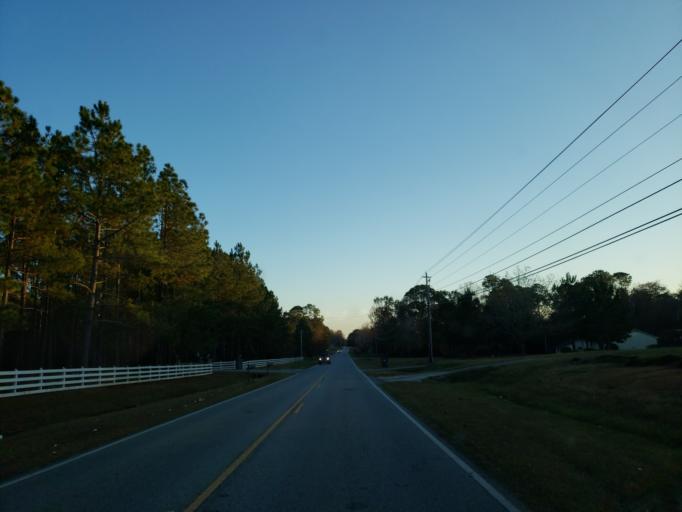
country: US
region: Georgia
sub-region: Crisp County
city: Cordele
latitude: 31.9410
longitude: -83.7659
